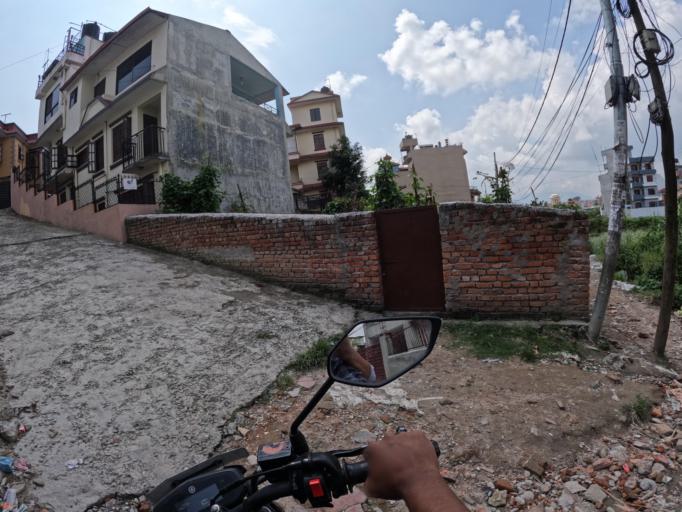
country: NP
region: Central Region
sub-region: Bagmati Zone
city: Patan
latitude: 27.6724
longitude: 85.3617
